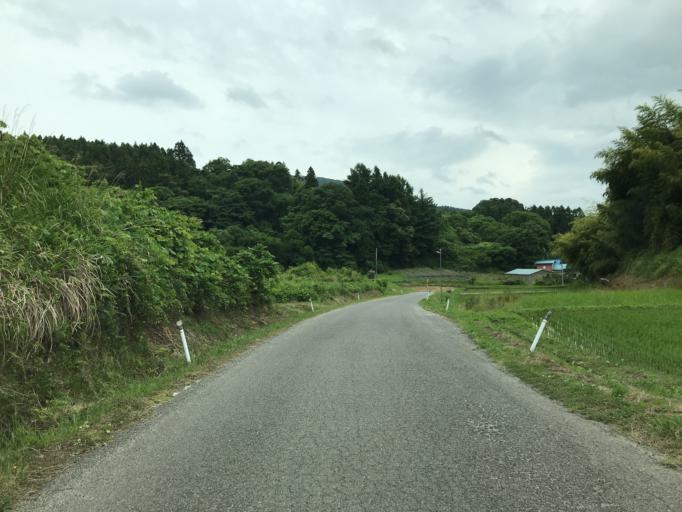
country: JP
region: Fukushima
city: Miharu
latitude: 37.3954
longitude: 140.5363
